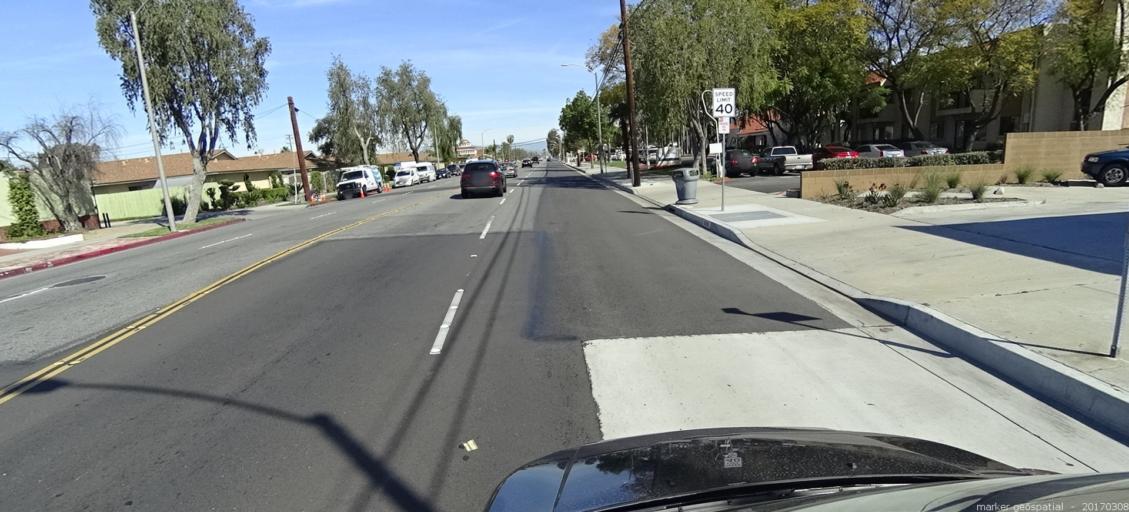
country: US
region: California
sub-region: Orange County
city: Stanton
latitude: 33.8326
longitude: -117.9847
